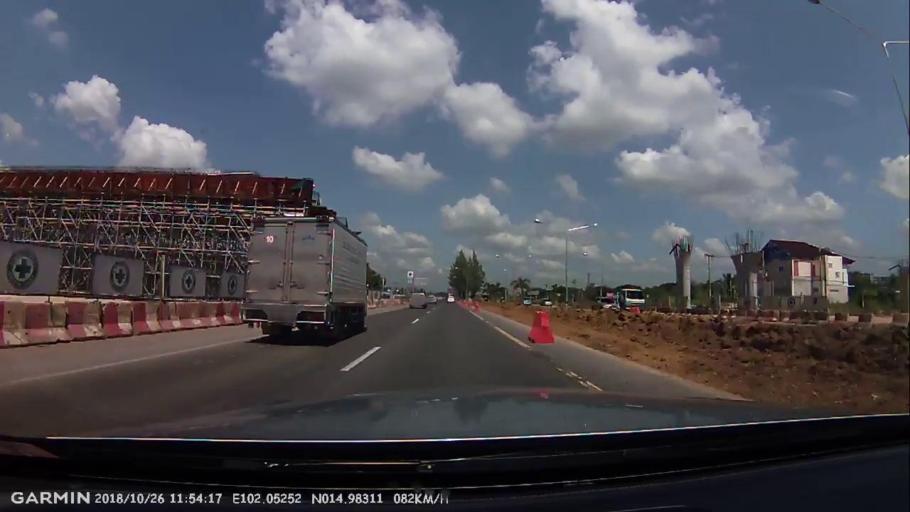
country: TH
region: Nakhon Ratchasima
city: Nakhon Ratchasima
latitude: 14.9833
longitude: 102.0525
